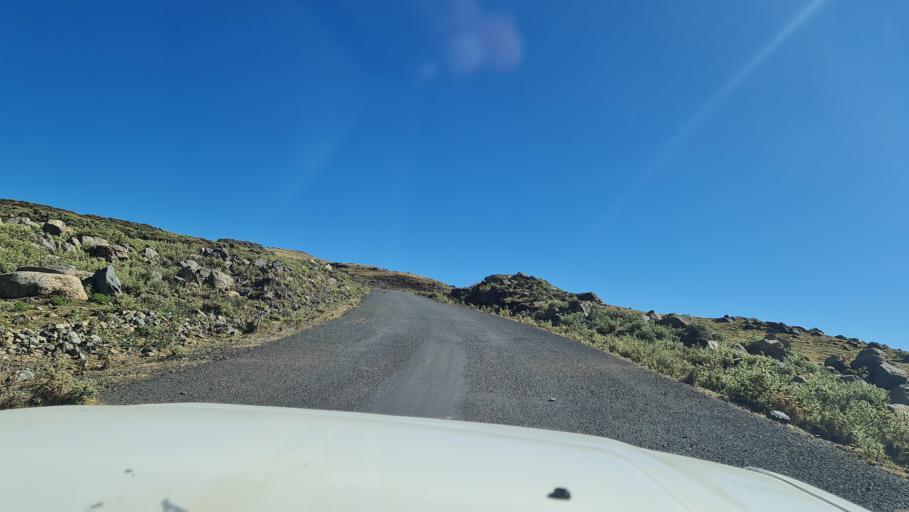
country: ET
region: Amhara
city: Debark'
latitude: 13.1346
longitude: 38.1756
